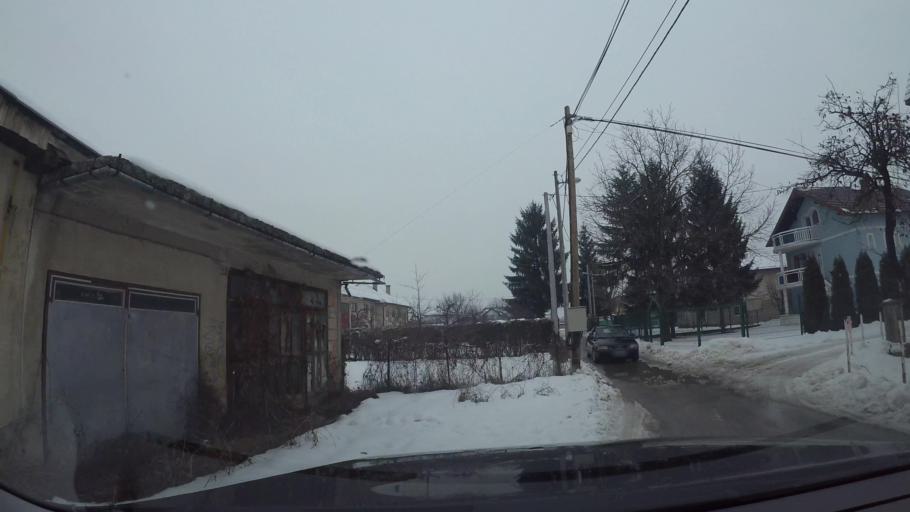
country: BA
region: Federation of Bosnia and Herzegovina
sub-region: Kanton Sarajevo
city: Sarajevo
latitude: 43.8351
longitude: 18.2830
